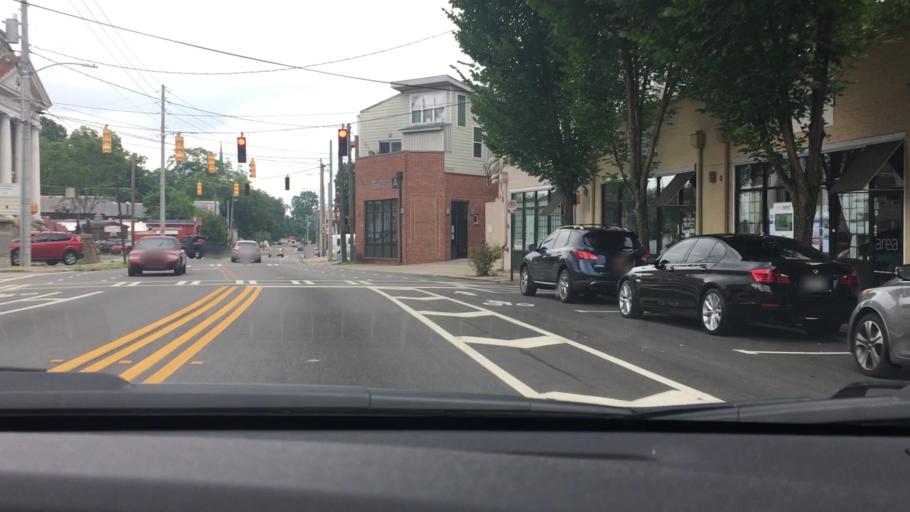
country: US
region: Georgia
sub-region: Fulton County
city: Atlanta
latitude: 33.7433
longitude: -84.4378
